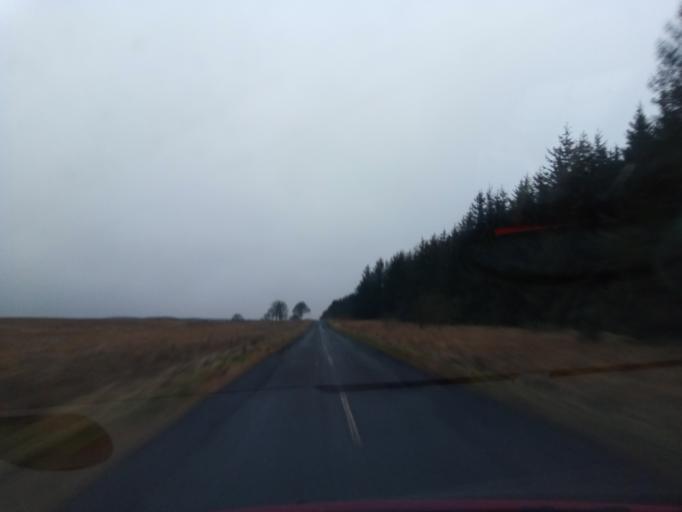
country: GB
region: England
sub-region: Northumberland
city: Rothley
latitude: 55.2072
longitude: -2.0308
